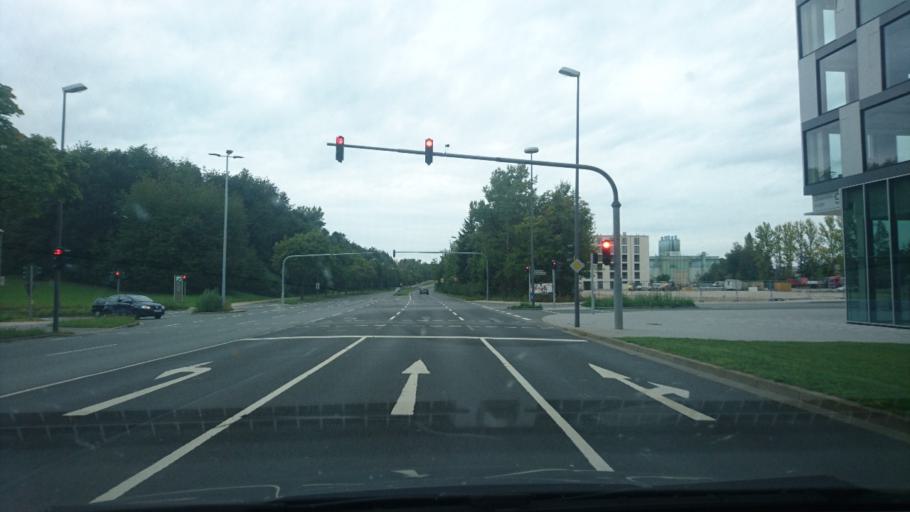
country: DE
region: Bavaria
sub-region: Upper Franconia
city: Bayreuth
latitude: 49.9274
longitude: 11.5914
